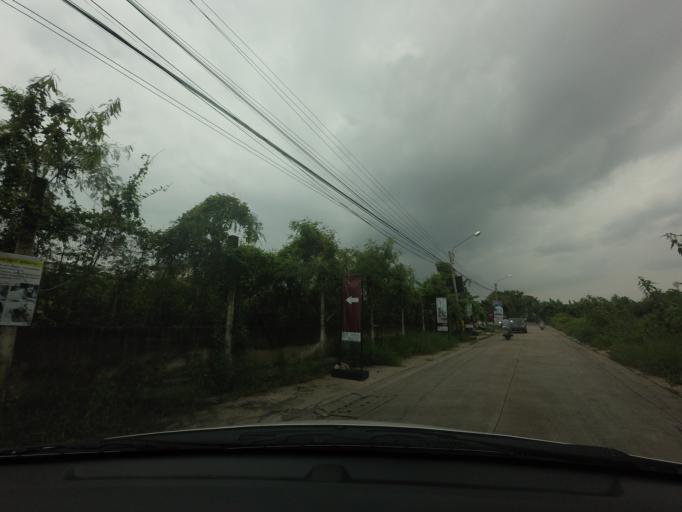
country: TH
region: Bangkok
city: Lak Si
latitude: 13.8984
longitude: 100.5719
